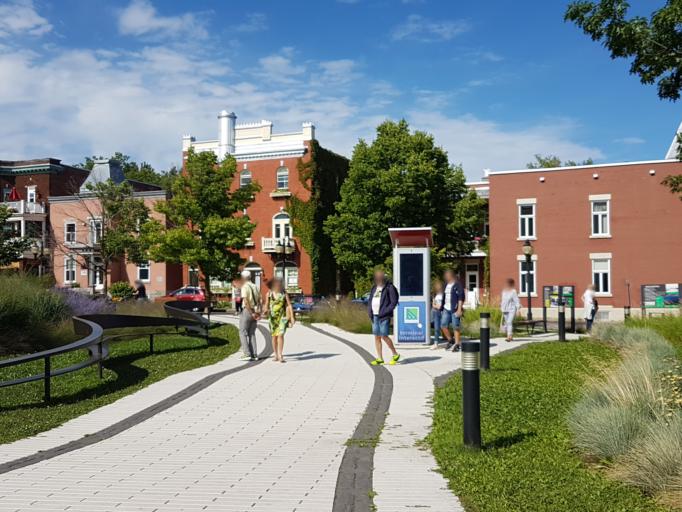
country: CA
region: Quebec
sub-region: Mauricie
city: Trois-Rivieres
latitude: 46.3418
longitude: -72.5385
